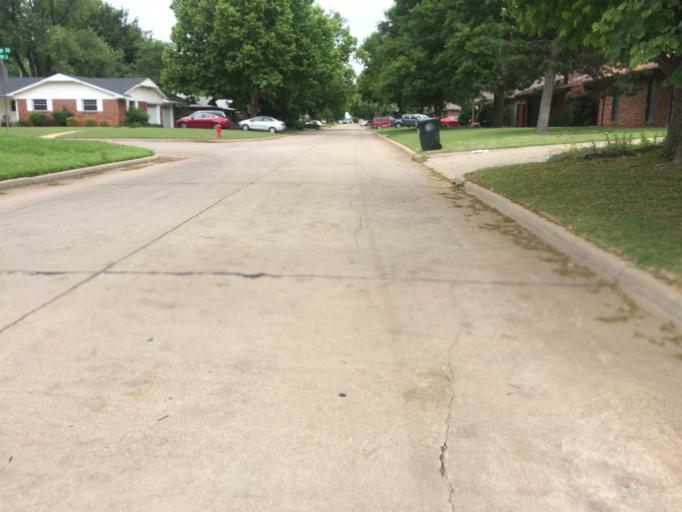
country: US
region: Oklahoma
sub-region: Cleveland County
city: Norman
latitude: 35.2143
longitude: -97.4787
